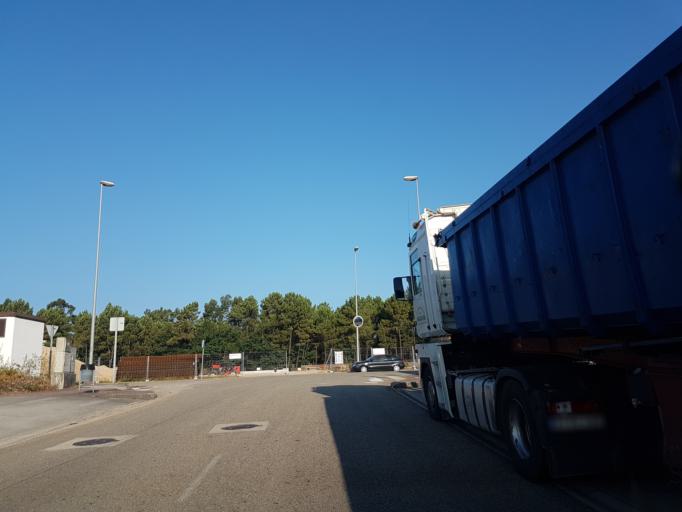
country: ES
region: Galicia
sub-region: Provincia de Pontevedra
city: Porrino
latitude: 42.1865
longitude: -8.6211
